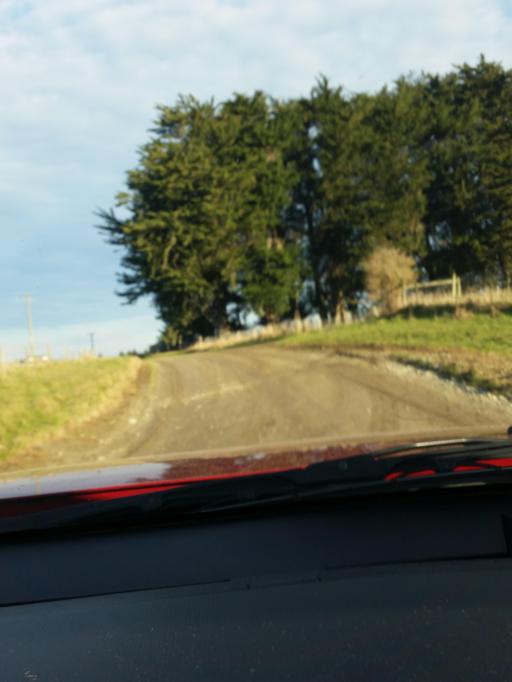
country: NZ
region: Southland
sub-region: Gore District
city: Gore
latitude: -46.2158
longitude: 168.7812
